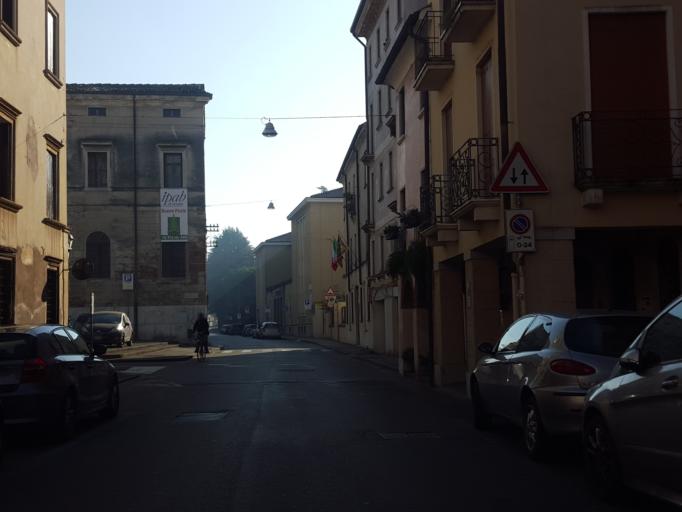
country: IT
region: Veneto
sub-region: Provincia di Vicenza
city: Vicenza
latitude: 45.5491
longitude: 11.5519
